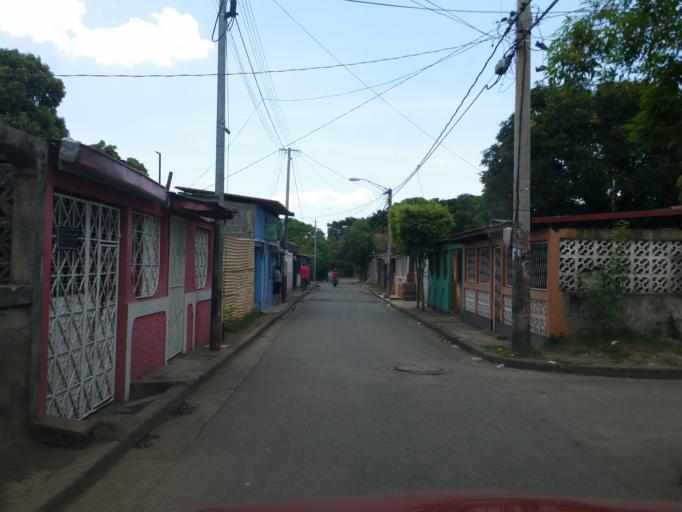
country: NI
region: Managua
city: Managua
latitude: 12.1274
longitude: -86.2465
